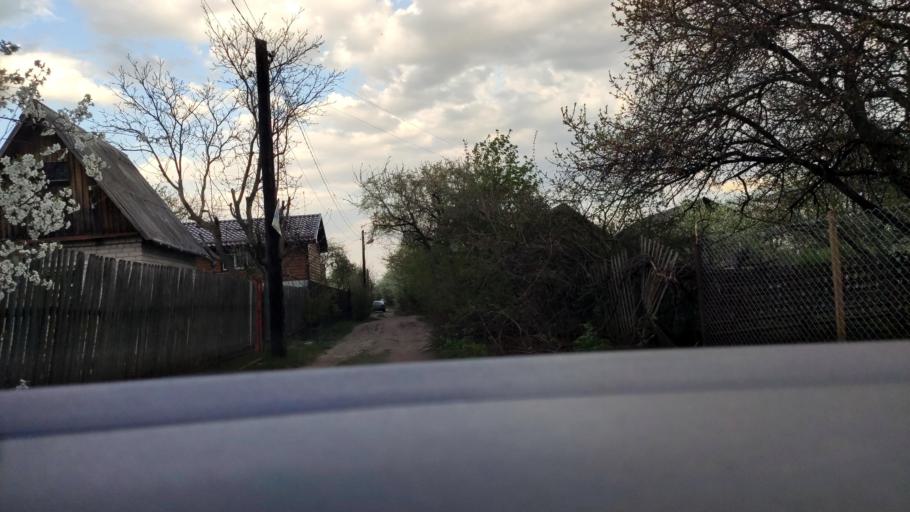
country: RU
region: Voronezj
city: Voronezh
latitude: 51.6086
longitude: 39.1522
